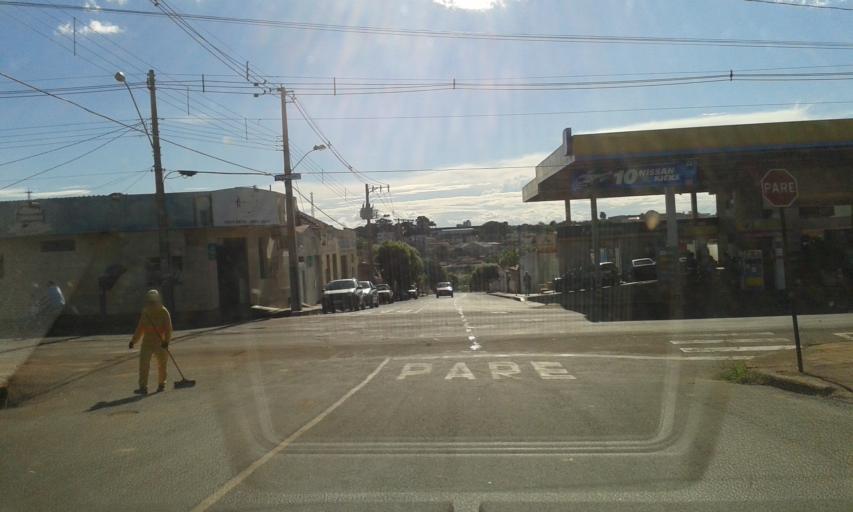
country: BR
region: Minas Gerais
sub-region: Ituiutaba
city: Ituiutaba
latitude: -18.9647
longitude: -49.4570
